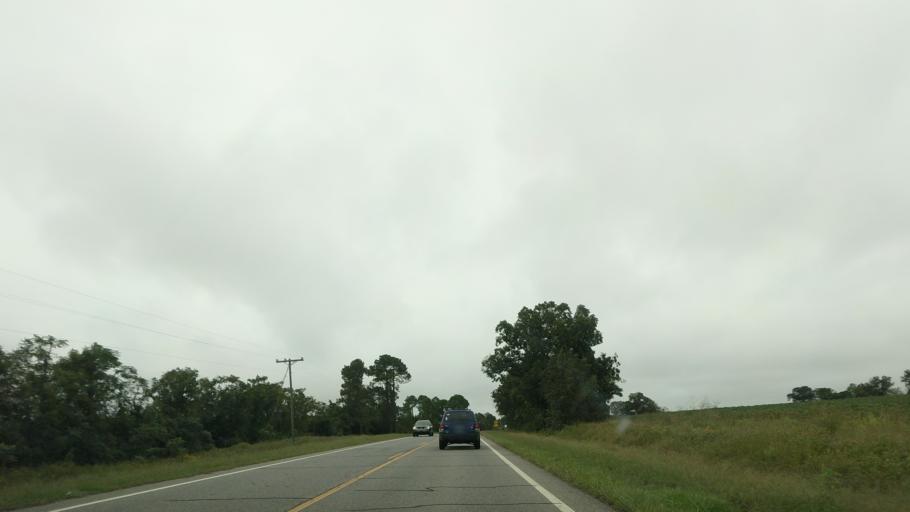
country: US
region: Georgia
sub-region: Irwin County
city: Ocilla
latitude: 31.5497
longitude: -83.2540
